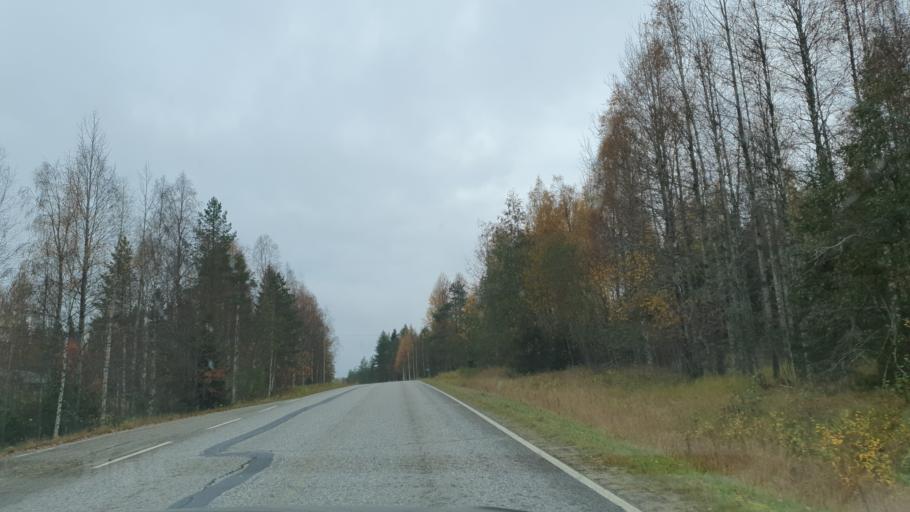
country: FI
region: Kainuu
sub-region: Kajaani
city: Sotkamo
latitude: 64.2916
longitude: 28.5087
